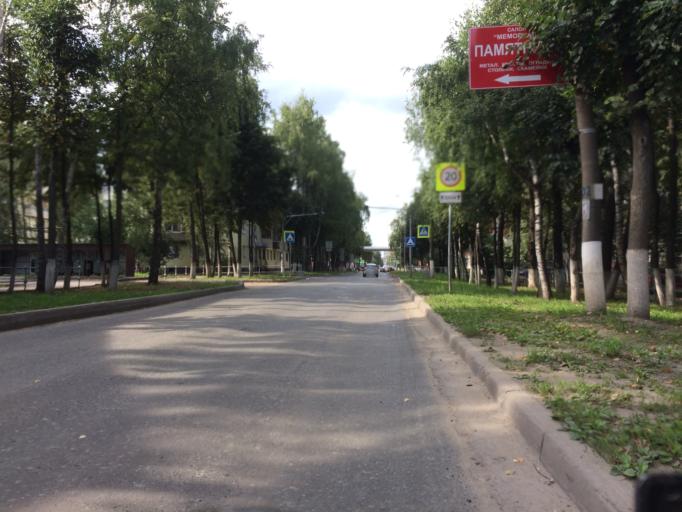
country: RU
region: Mariy-El
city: Yoshkar-Ola
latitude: 56.6304
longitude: 47.8780
